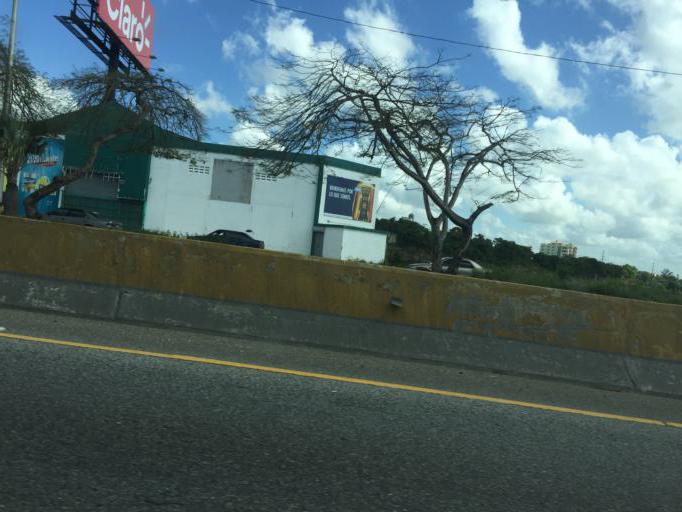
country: DO
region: Santo Domingo
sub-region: Santo Domingo
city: Santo Domingo Este
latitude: 18.4756
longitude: -69.8349
